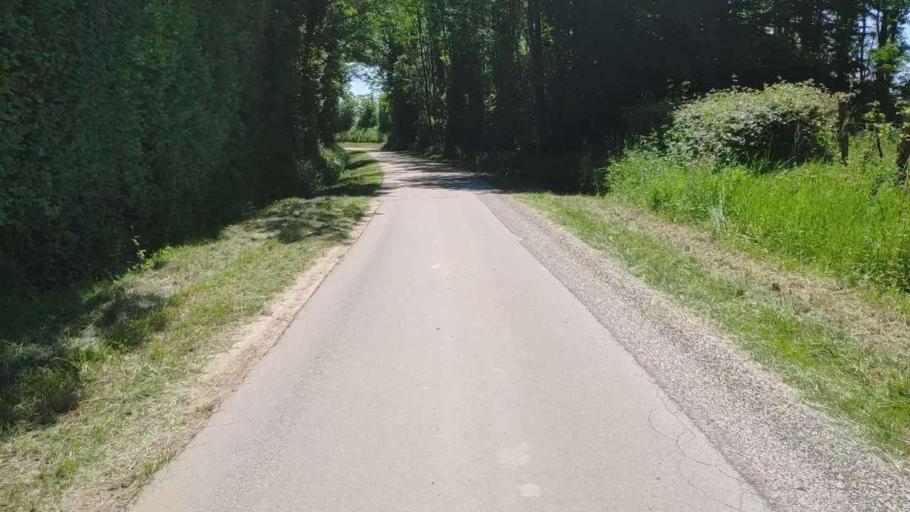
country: FR
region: Franche-Comte
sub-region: Departement du Jura
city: Bletterans
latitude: 46.7533
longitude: 5.4030
